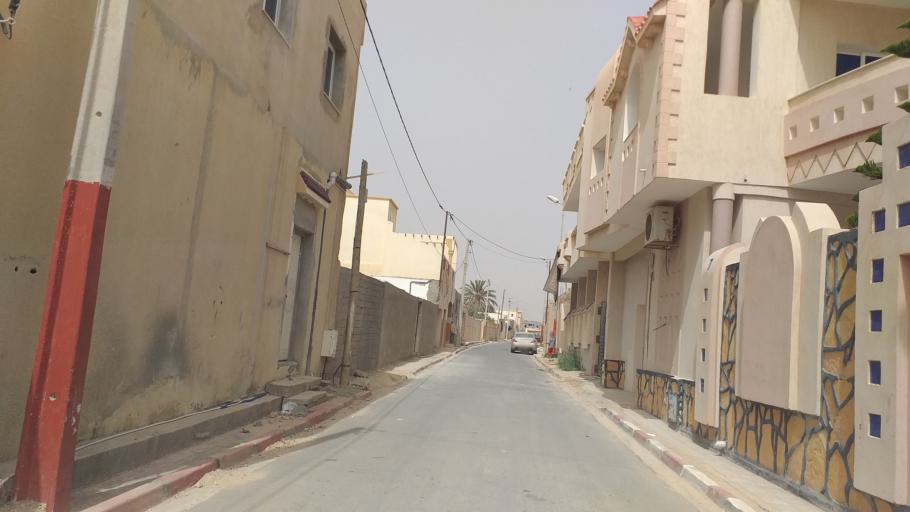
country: TN
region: Qabis
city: Gabes
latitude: 33.9410
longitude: 10.0608
